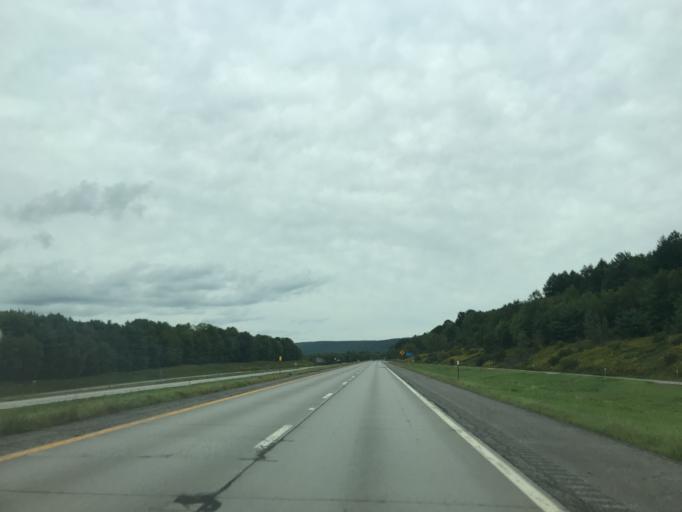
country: US
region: New York
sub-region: Otsego County
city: Oneonta
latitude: 42.4826
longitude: -74.9665
